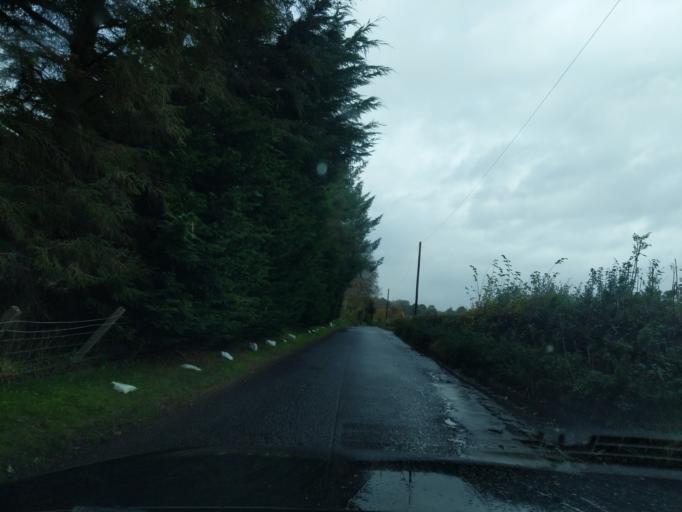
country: GB
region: Scotland
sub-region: Edinburgh
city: Balerno
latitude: 55.9155
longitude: -3.3482
